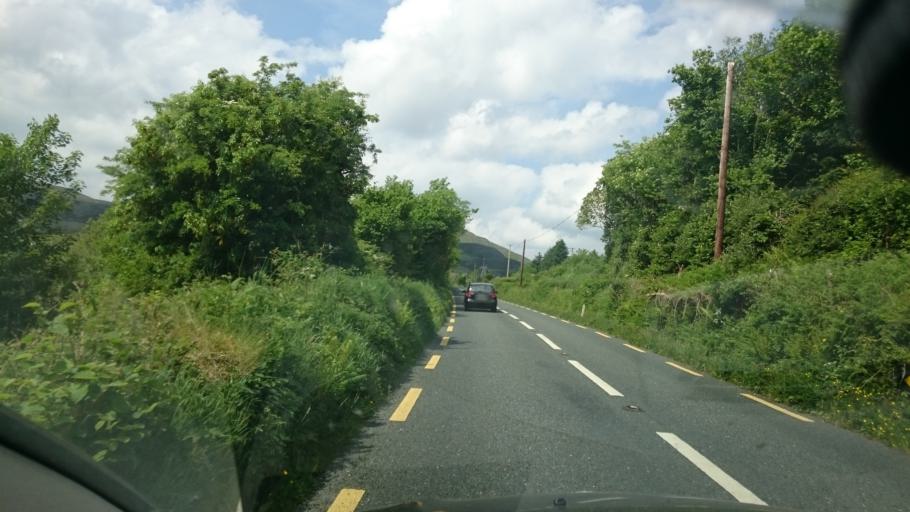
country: IE
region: Connaught
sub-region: Maigh Eo
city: Swinford
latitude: 54.0886
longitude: -8.9316
